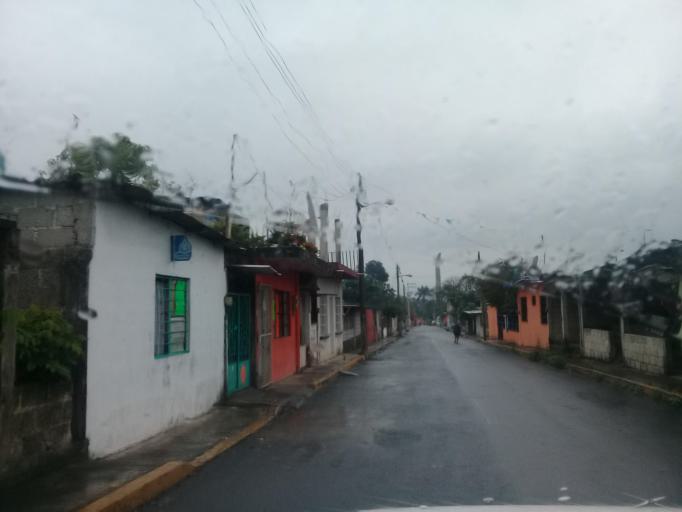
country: MX
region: Veracruz
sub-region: Cordoba
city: San Jose de Tapia
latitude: 18.8498
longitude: -96.9499
